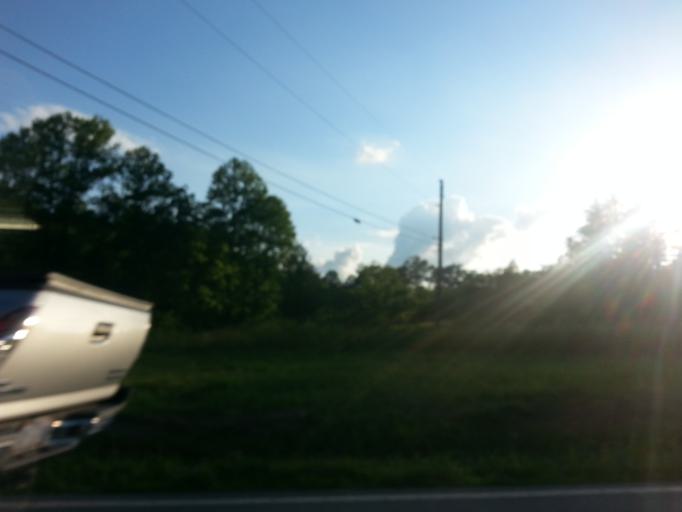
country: US
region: North Carolina
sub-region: Cherokee County
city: Murphy
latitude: 35.0332
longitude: -84.1409
